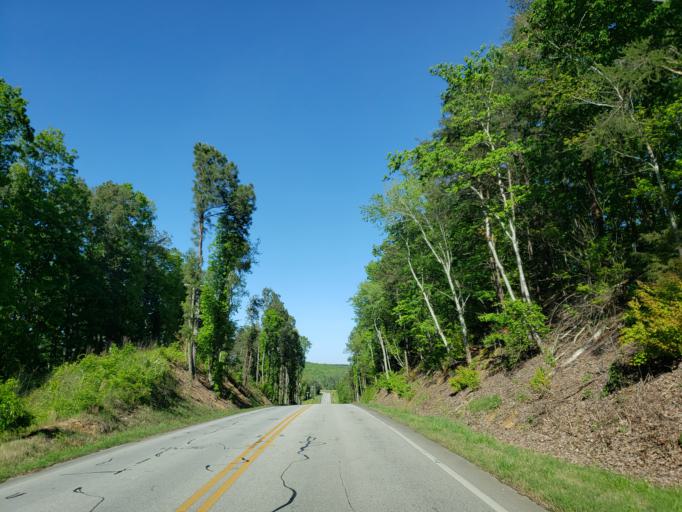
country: US
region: Georgia
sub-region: Polk County
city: Cedartown
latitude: 33.9095
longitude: -85.3077
